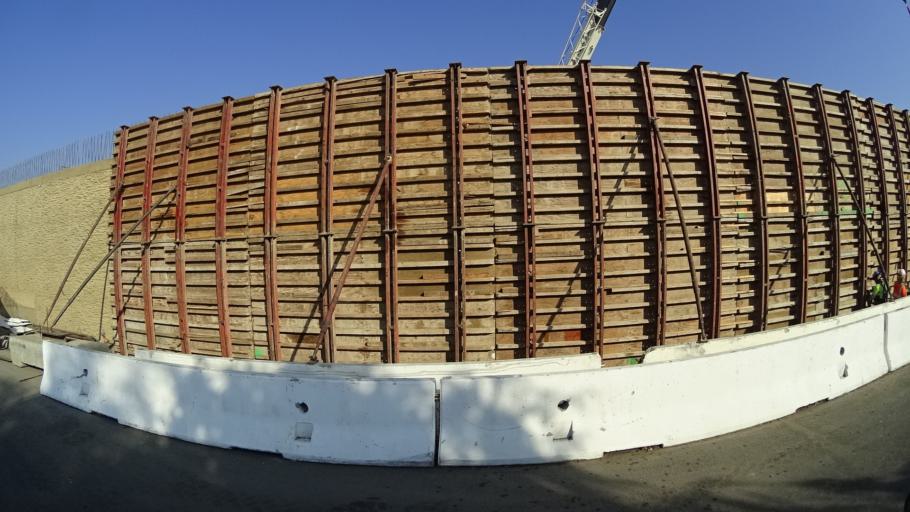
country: US
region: California
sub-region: Kern County
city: Bakersfield
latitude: 35.3643
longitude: -119.0539
